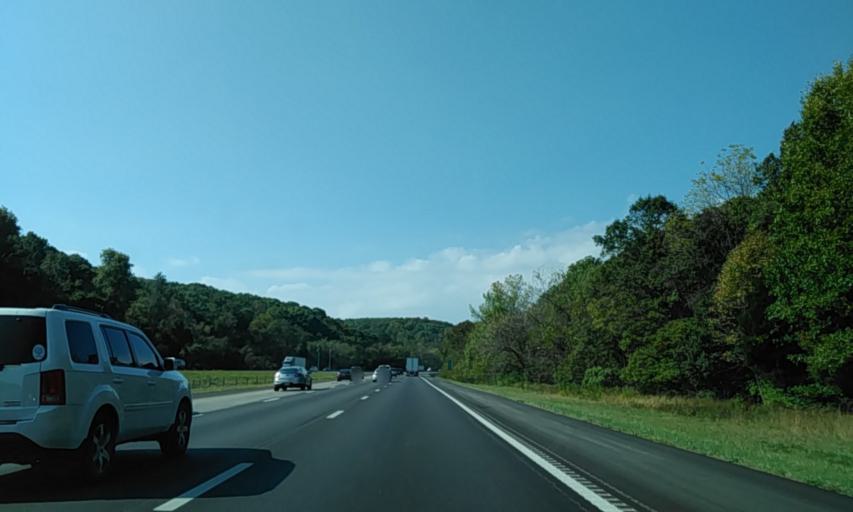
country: US
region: Missouri
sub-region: Saint Louis County
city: Valley Park
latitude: 38.5301
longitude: -90.5297
